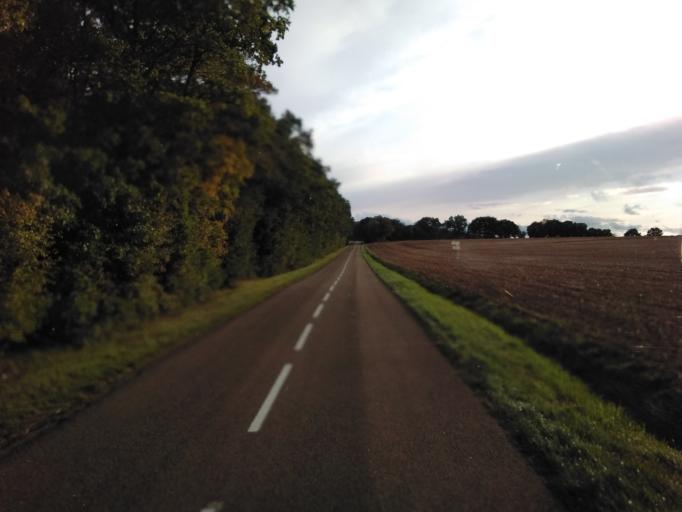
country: FR
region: Bourgogne
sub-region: Departement de l'Yonne
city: Ravieres
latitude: 47.8152
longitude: 4.3628
